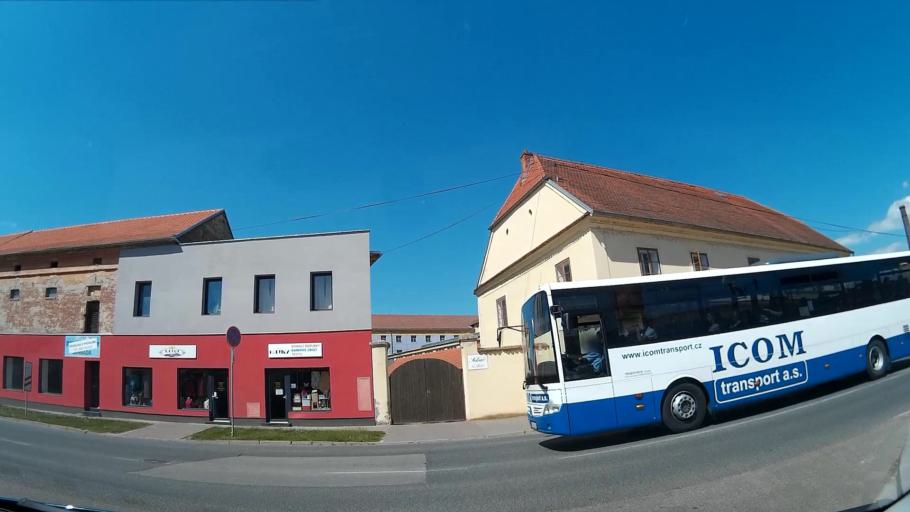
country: CZ
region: South Moravian
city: Ivancice
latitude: 49.0994
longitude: 16.3757
